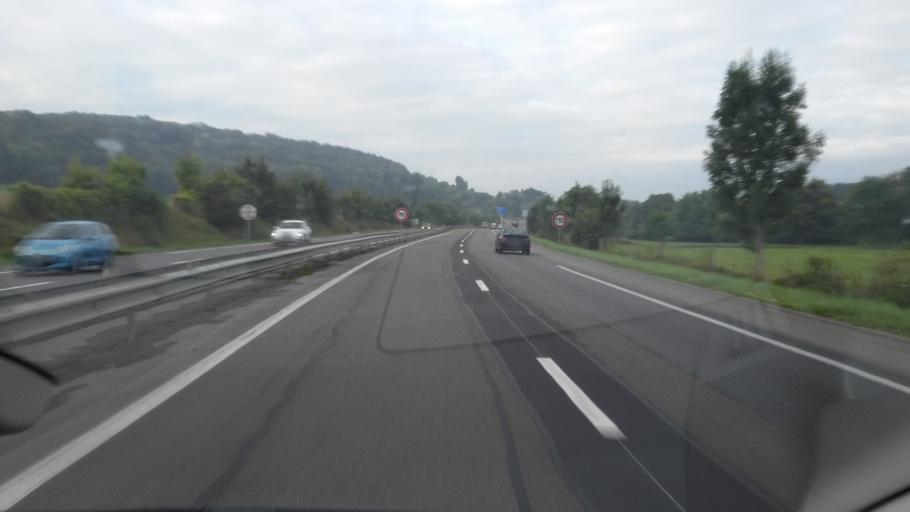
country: FR
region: Champagne-Ardenne
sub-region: Departement des Ardennes
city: La Francheville
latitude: 49.6844
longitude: 4.6701
